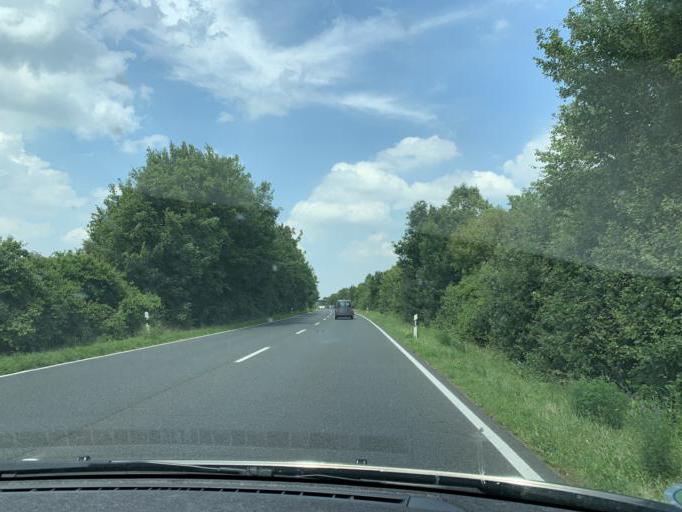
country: DE
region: North Rhine-Westphalia
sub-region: Regierungsbezirk Koln
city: Eschweiler
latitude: 50.8449
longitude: 6.2433
